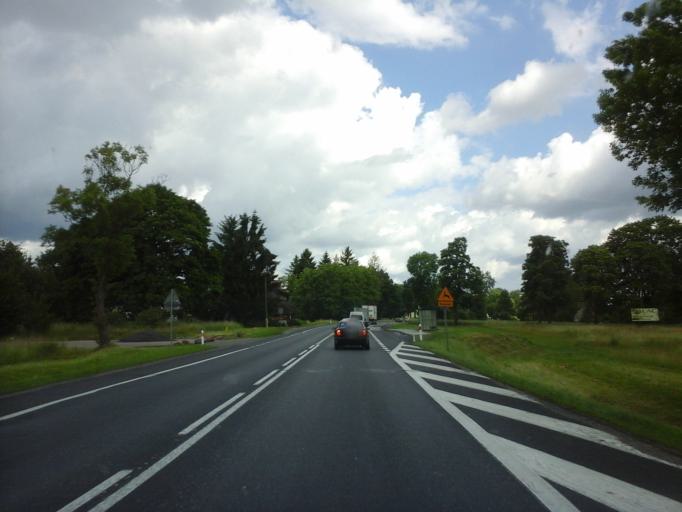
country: PL
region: West Pomeranian Voivodeship
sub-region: Powiat bialogardzki
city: Bialogard
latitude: 54.1062
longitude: 15.9973
